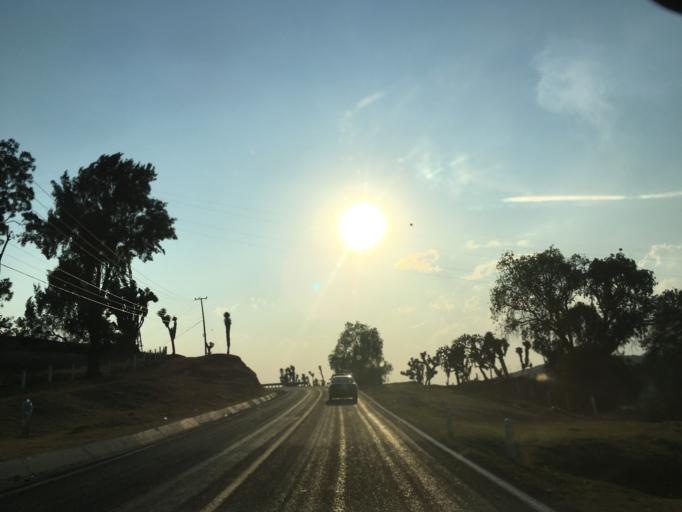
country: MX
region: Michoacan
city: Charo
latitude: 19.7442
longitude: -101.0732
